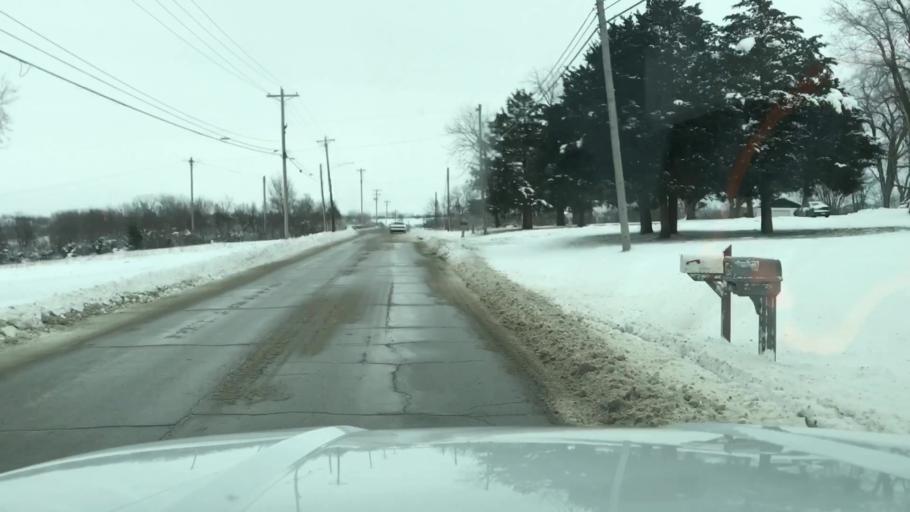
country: US
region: Missouri
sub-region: Clinton County
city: Cameron
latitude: 39.7424
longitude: -94.2221
